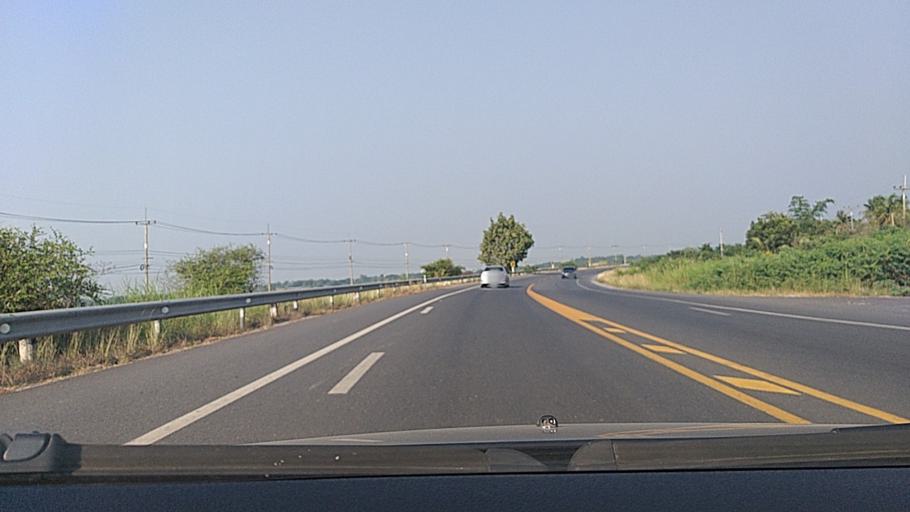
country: TH
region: Sing Buri
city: Phrom Buri
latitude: 14.7837
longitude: 100.4347
